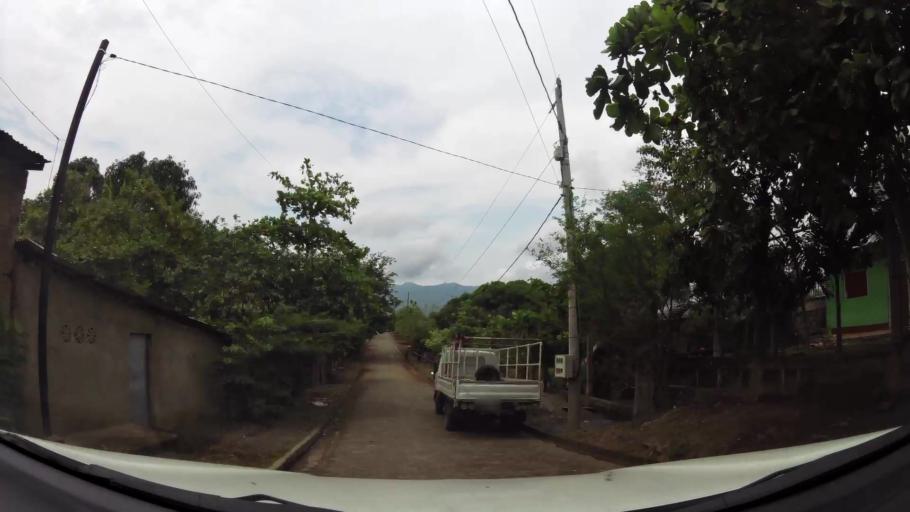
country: NI
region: Granada
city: Granada
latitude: 11.9149
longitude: -85.9590
